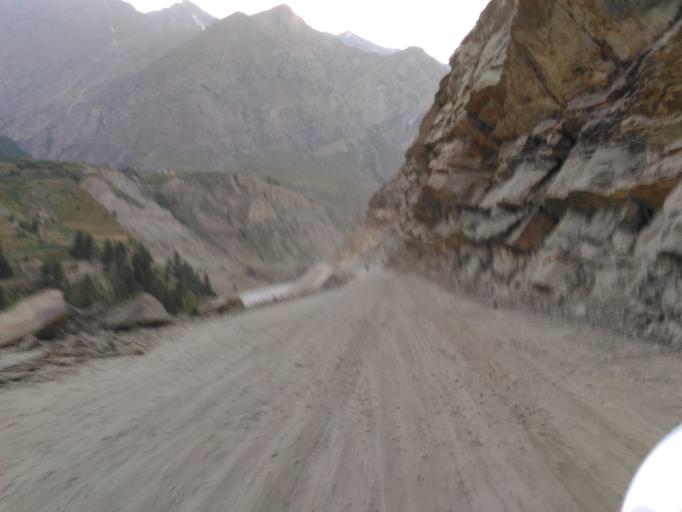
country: IN
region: Himachal Pradesh
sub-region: Lahul and Spiti
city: Kyelang
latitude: 32.5182
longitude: 76.9791
